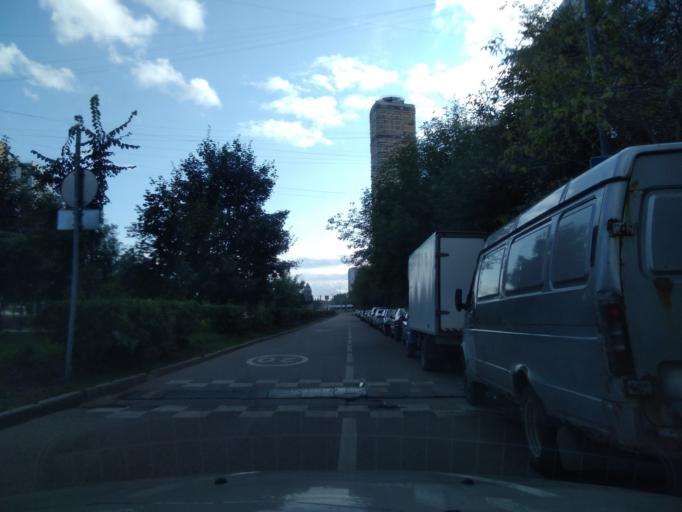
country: RU
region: Moscow
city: Strogino
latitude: 55.8071
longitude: 37.4171
